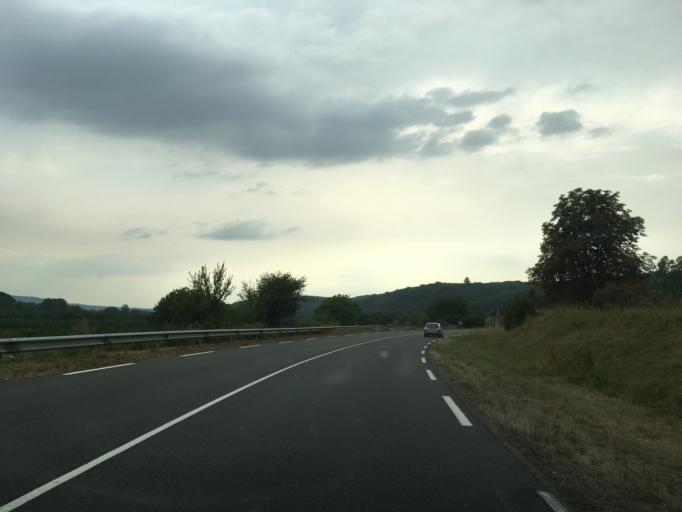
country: FR
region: Aquitaine
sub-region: Departement de la Dordogne
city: Carsac-Aillac
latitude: 44.8515
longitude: 1.3313
